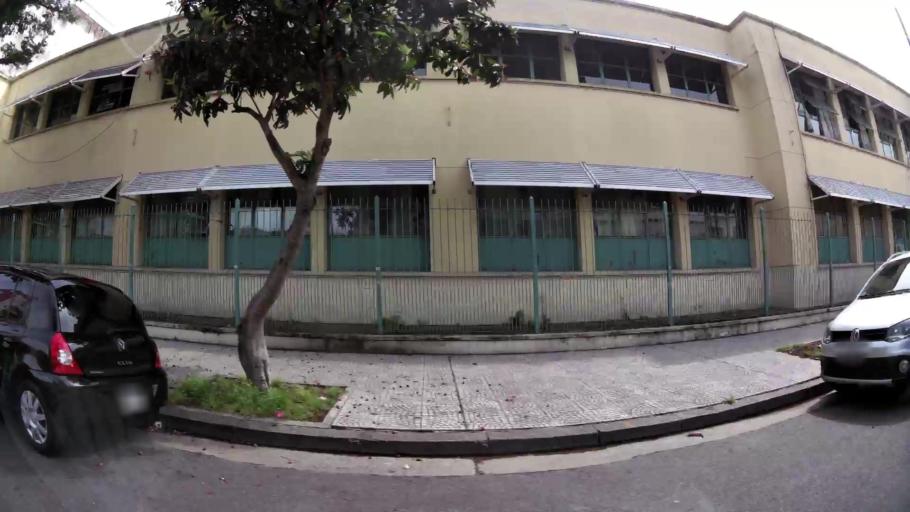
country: AR
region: Buenos Aires F.D.
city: Villa Santa Rita
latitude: -34.6208
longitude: -58.5162
